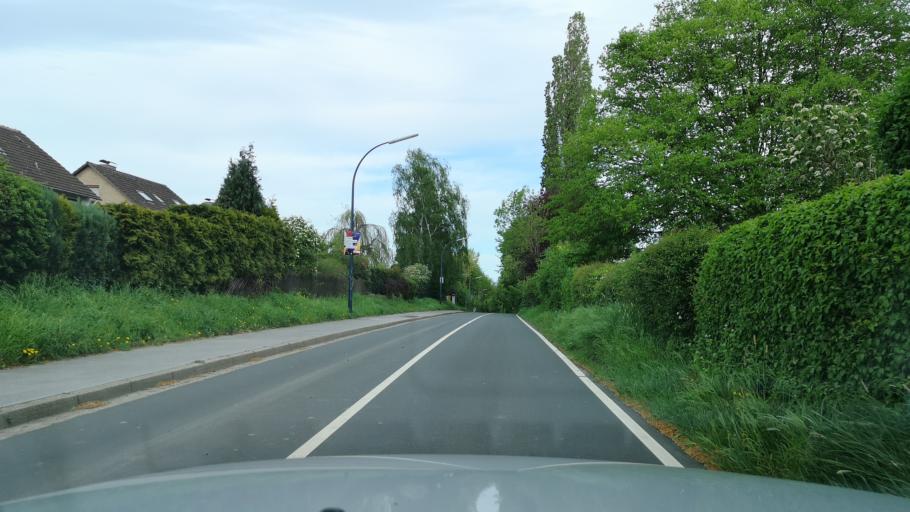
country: DE
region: North Rhine-Westphalia
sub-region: Regierungsbezirk Arnsberg
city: Holzwickede
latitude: 51.4884
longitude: 7.6409
